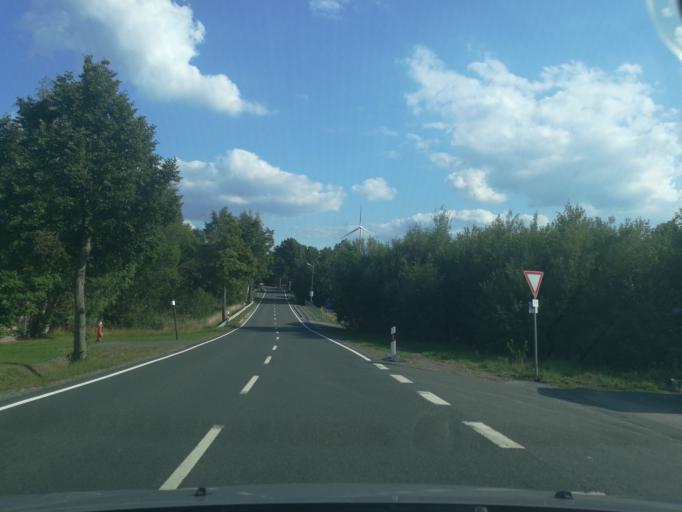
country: DE
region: Saxony
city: Eichigt
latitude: 50.3258
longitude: 12.1564
